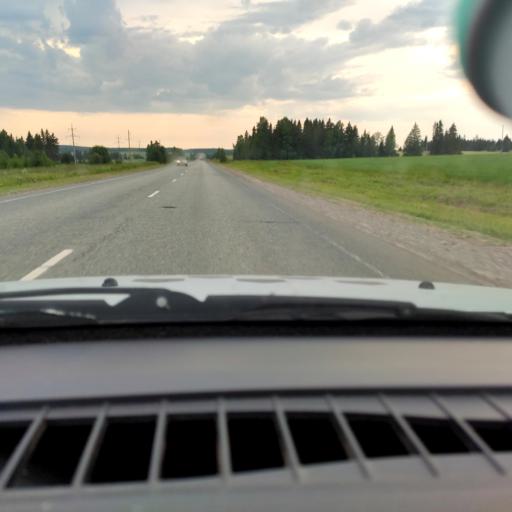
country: RU
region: Udmurtiya
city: Debesy
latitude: 57.6119
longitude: 53.5483
